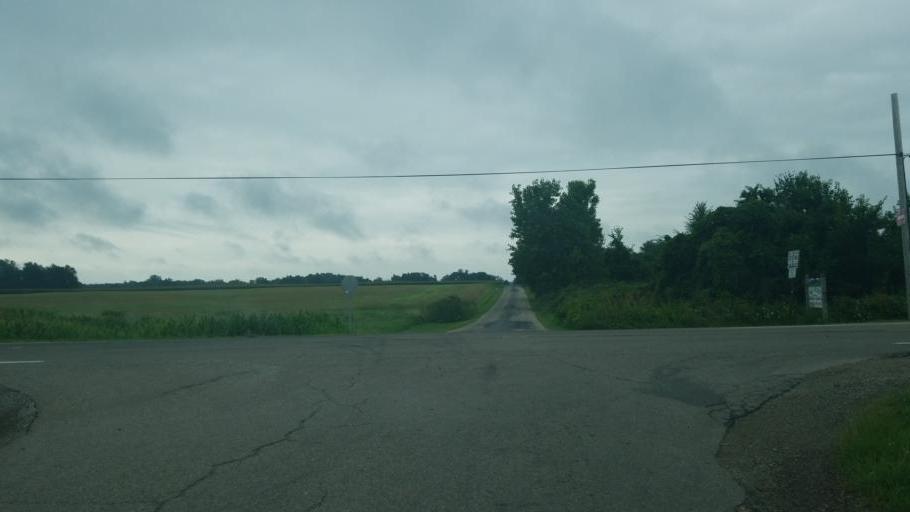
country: US
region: Ohio
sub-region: Knox County
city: Centerburg
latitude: 40.4004
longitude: -82.7405
